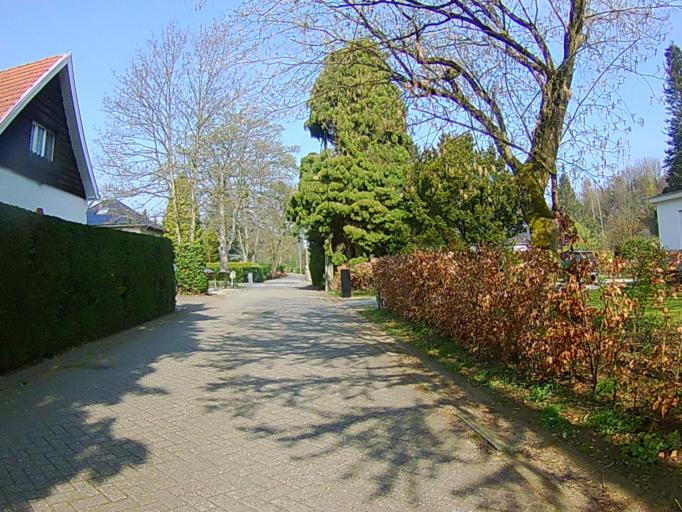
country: BE
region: Flanders
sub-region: Provincie Antwerpen
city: Kapellen
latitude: 51.3036
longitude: 4.4422
